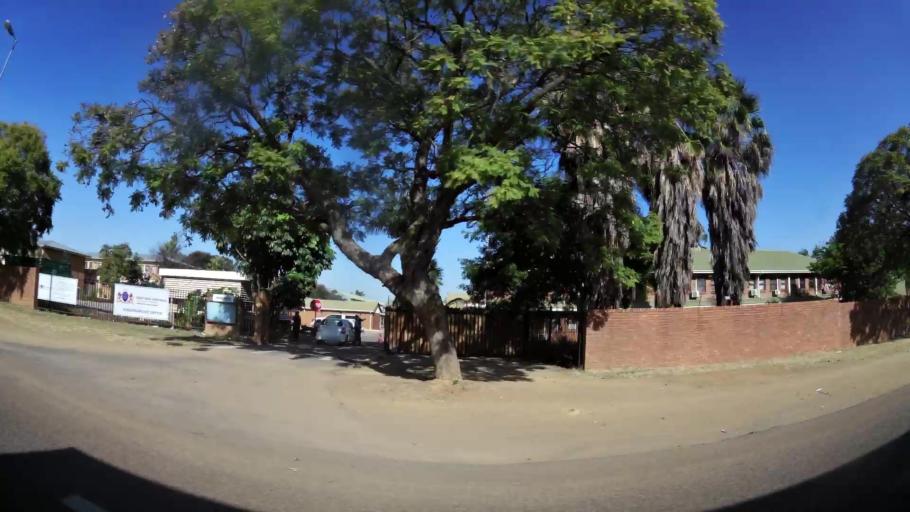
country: ZA
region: Gauteng
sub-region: City of Tshwane Metropolitan Municipality
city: Pretoria
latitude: -25.7149
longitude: 28.2515
